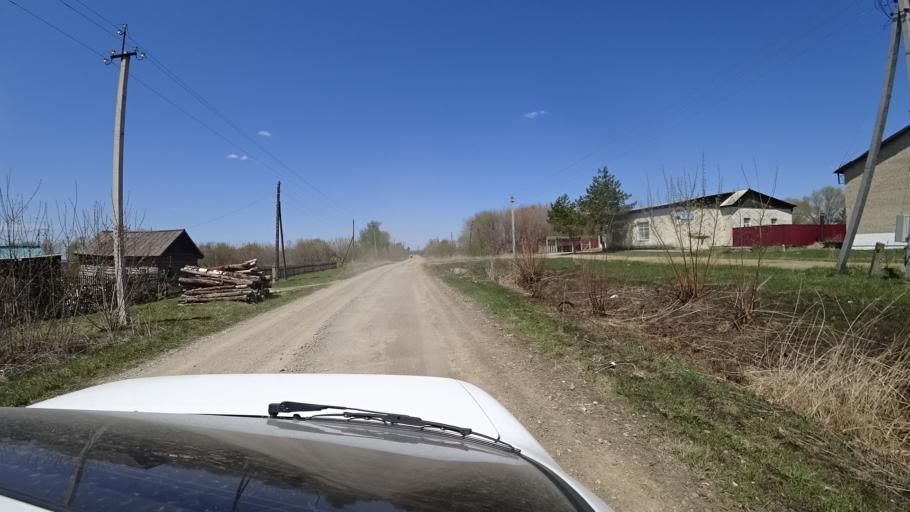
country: RU
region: Primorskiy
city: Lazo
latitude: 45.7964
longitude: 133.7650
